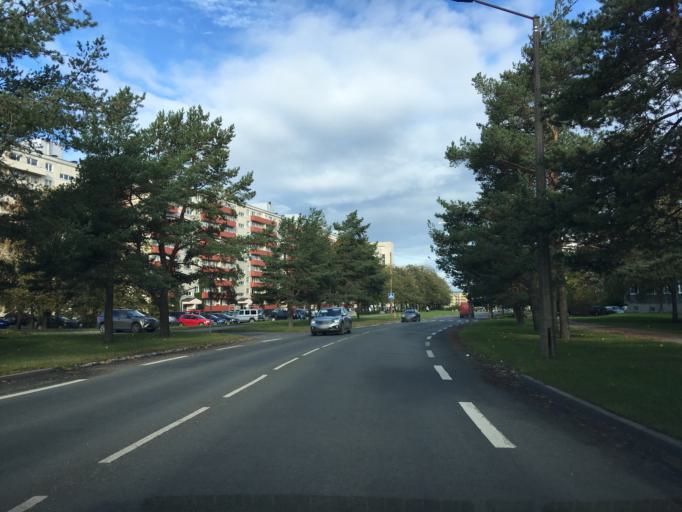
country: EE
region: Harju
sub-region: Tallinna linn
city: Tallinn
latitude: 59.3961
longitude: 24.6827
